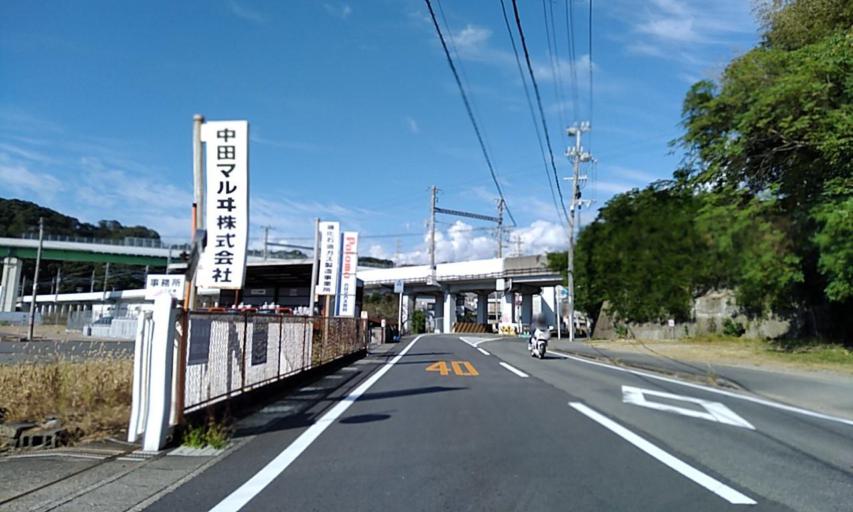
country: JP
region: Wakayama
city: Tanabe
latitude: 33.7499
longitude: 135.3523
